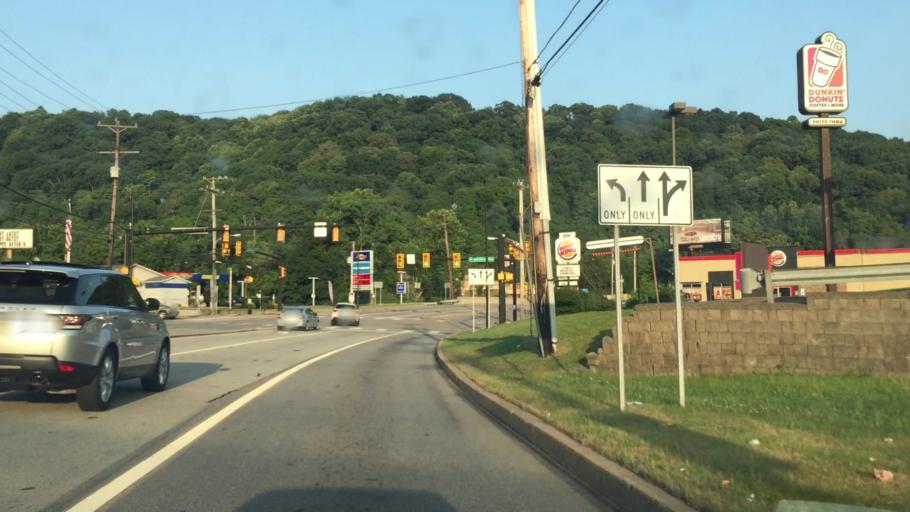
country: US
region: Pennsylvania
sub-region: Allegheny County
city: Etna
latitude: 40.5118
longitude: -79.9483
